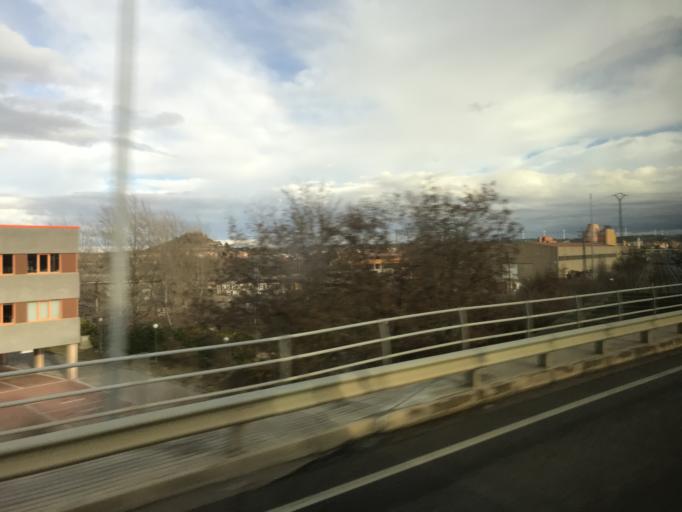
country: ES
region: Castille and Leon
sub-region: Provincia de Palencia
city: Palencia
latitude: 42.0281
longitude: -4.5510
